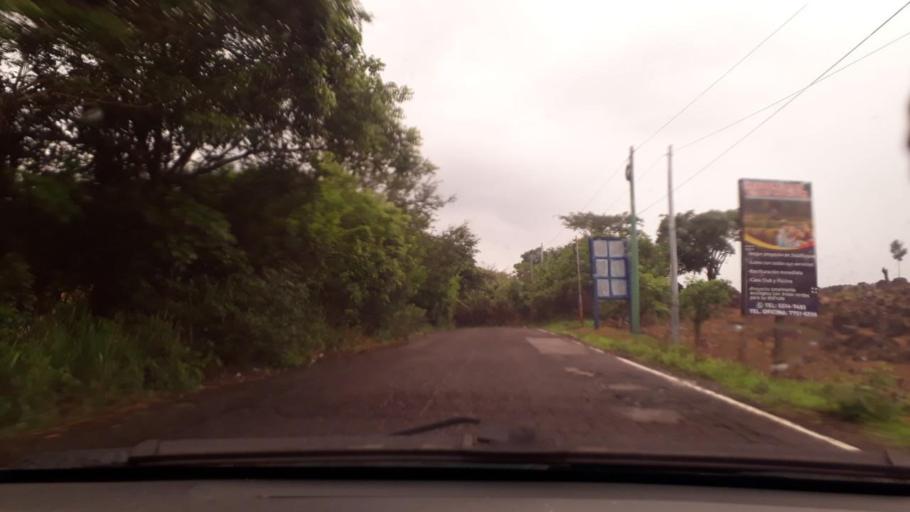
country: GT
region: Jutiapa
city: Comapa
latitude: 14.0378
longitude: -89.9150
